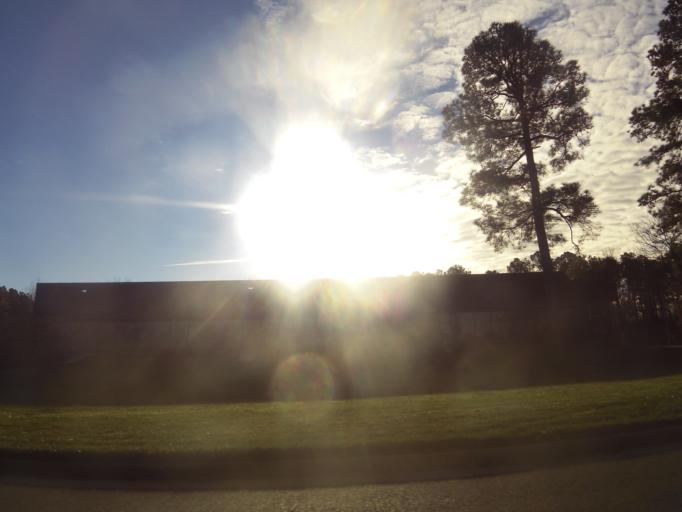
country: US
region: Virginia
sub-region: Henrico County
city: Short Pump
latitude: 37.6548
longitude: -77.5782
